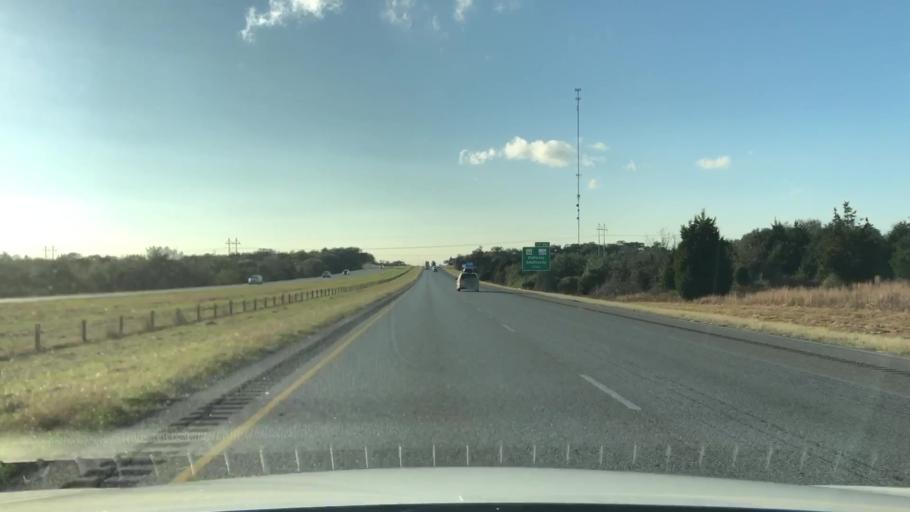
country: US
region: Texas
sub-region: Fayette County
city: Flatonia
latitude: 29.6974
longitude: -97.0806
